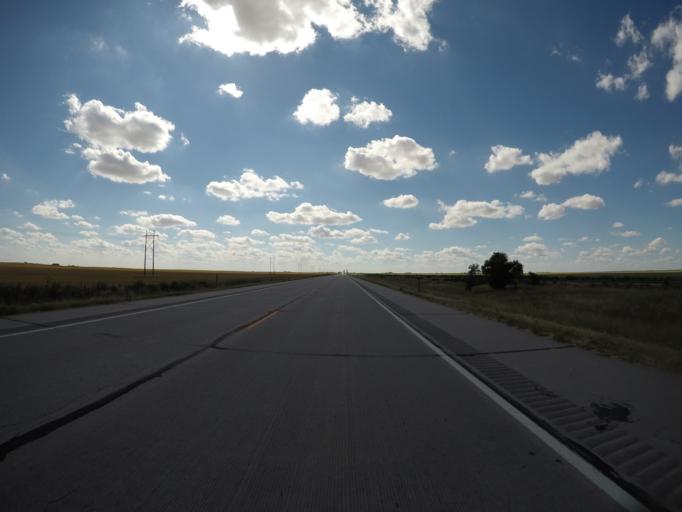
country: US
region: Colorado
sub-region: Phillips County
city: Holyoke
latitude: 40.6038
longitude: -102.4196
